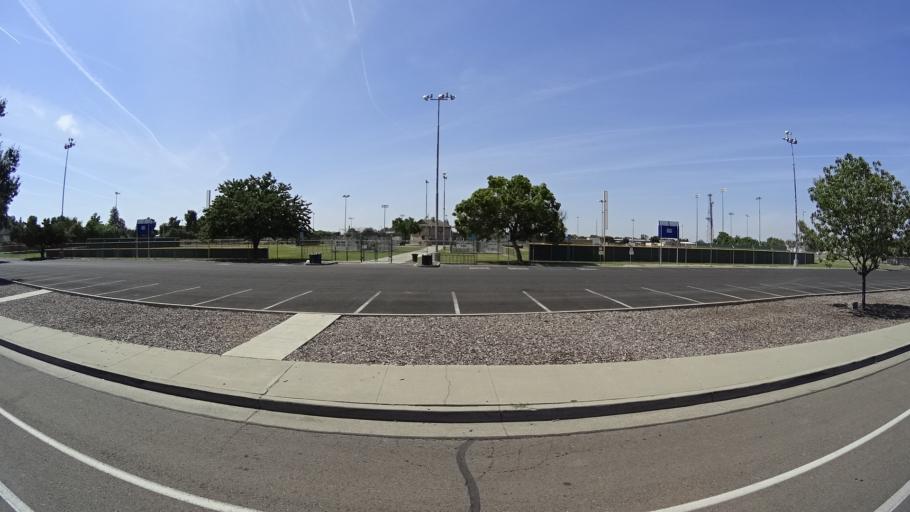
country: US
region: California
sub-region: Kings County
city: Hanford
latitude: 36.3359
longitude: -119.6647
